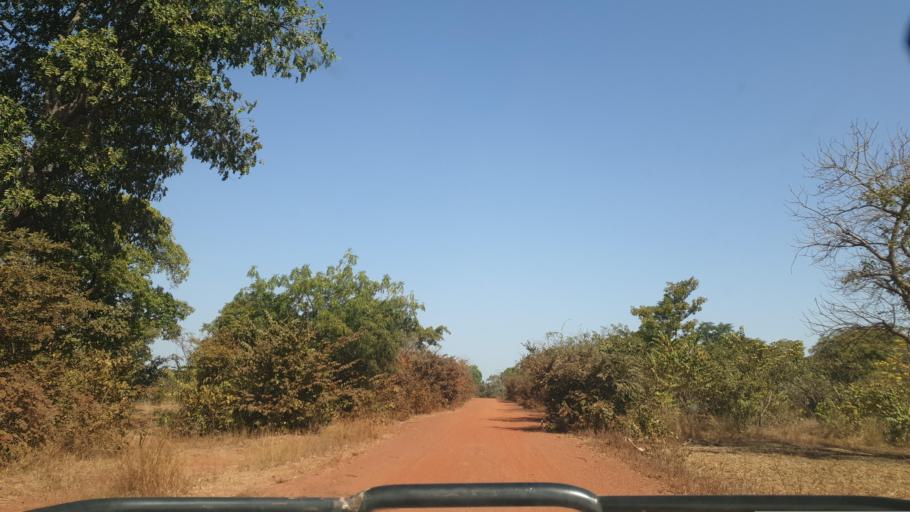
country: ML
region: Sikasso
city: Bougouni
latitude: 11.8397
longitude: -6.9782
